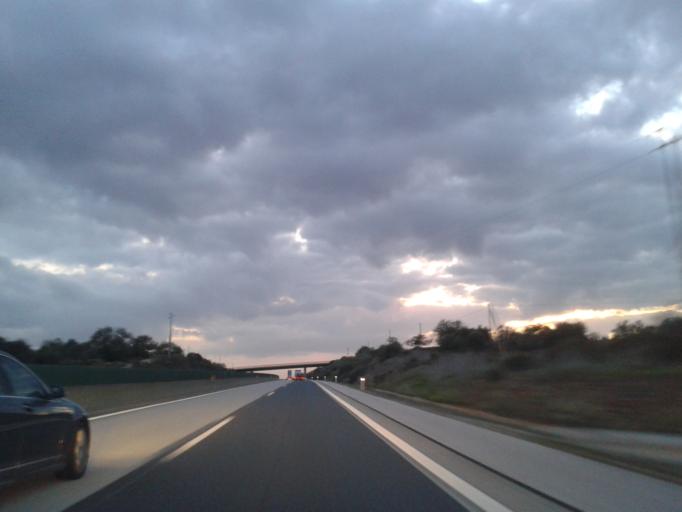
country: PT
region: Faro
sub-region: Albufeira
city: Ferreiras
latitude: 37.1436
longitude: -8.2240
